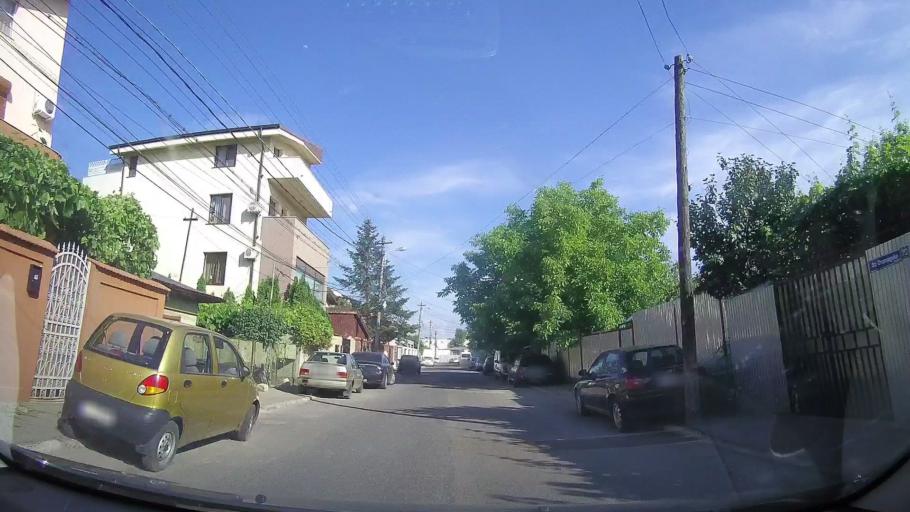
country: RO
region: Bucuresti
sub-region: Municipiul Bucuresti
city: Bucharest
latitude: 44.4084
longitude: 26.1347
